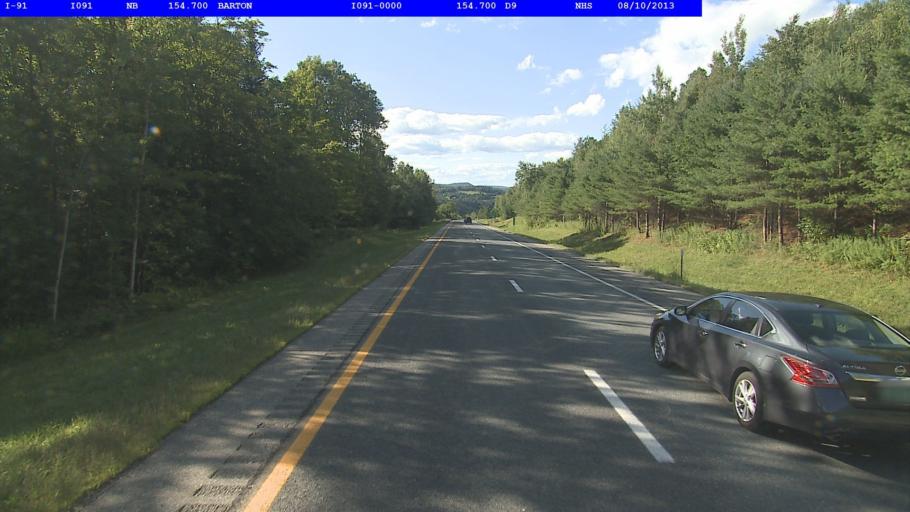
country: US
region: Vermont
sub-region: Orleans County
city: Newport
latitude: 44.7188
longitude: -72.1764
